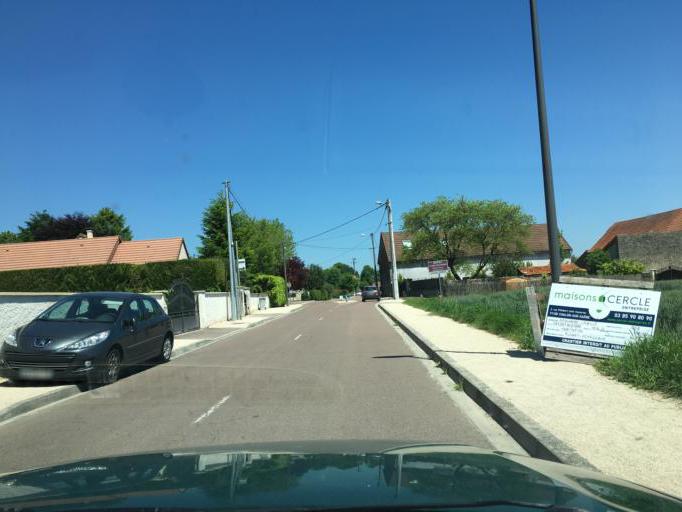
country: FR
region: Bourgogne
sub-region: Departement de la Cote-d'Or
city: Nuits-Saint-Georges
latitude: 47.1680
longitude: 4.9822
